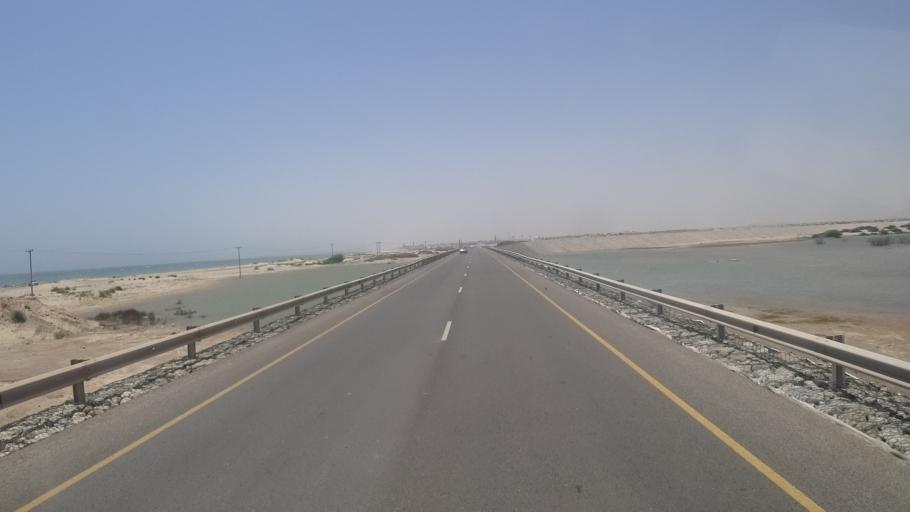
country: OM
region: Ash Sharqiyah
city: Sur
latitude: 22.0943
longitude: 59.6956
